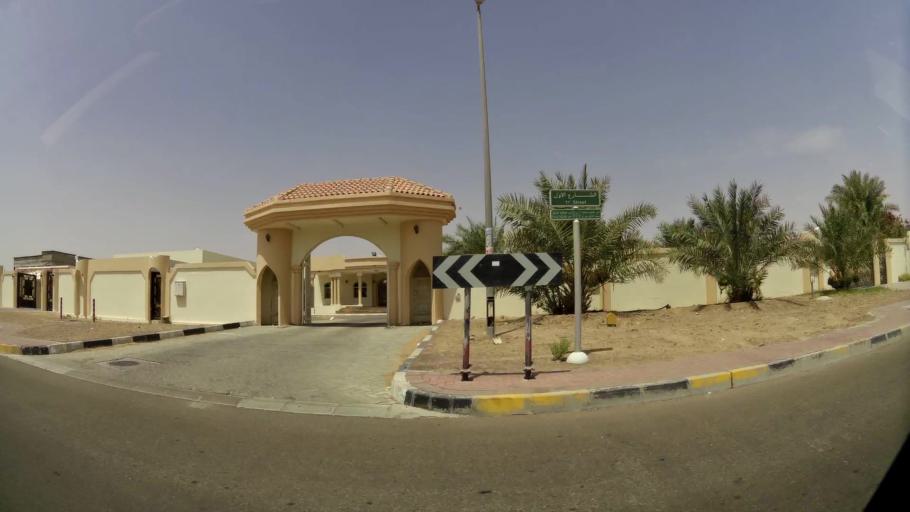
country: AE
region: Abu Dhabi
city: Al Ain
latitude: 24.1853
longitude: 55.7241
